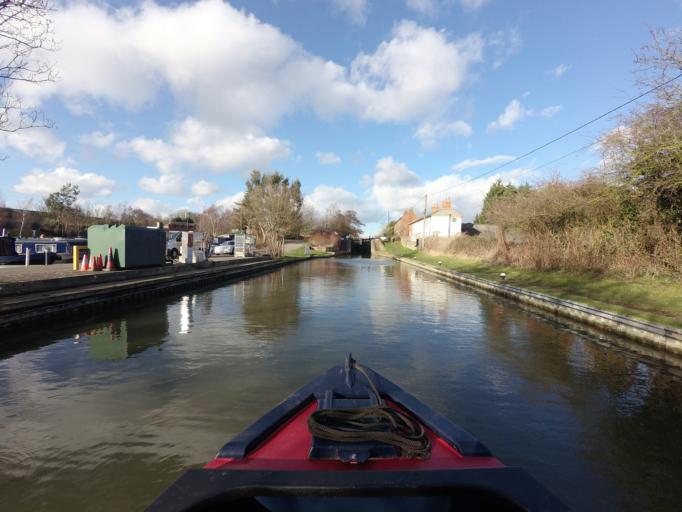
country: GB
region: England
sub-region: Northamptonshire
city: Long Buckby
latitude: 52.2728
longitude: -1.0950
